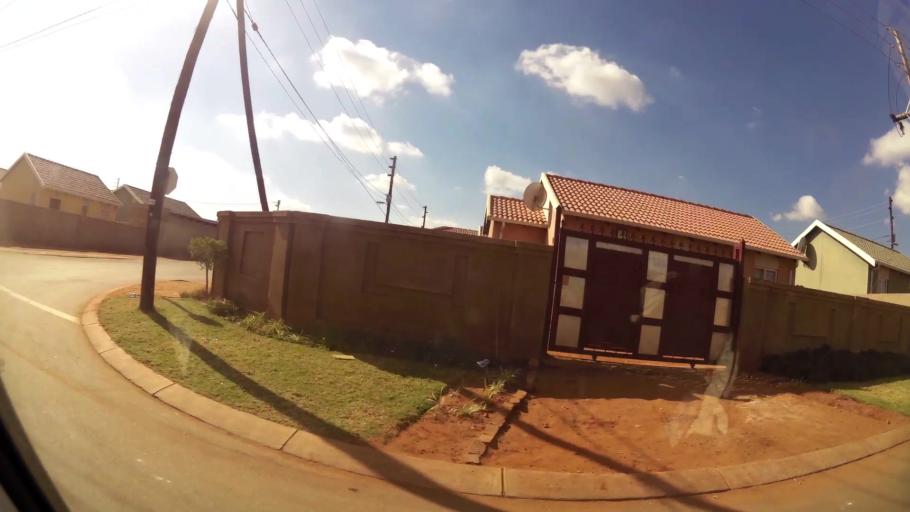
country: ZA
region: Gauteng
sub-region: City of Tshwane Metropolitan Municipality
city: Cullinan
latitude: -25.6875
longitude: 28.4062
